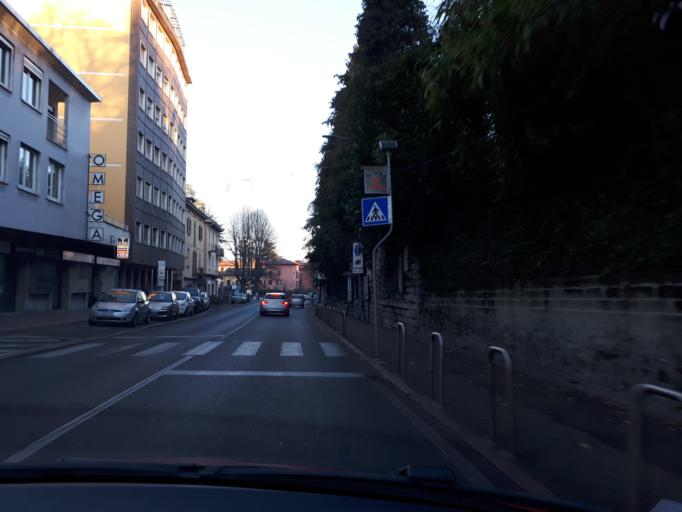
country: IT
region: Lombardy
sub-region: Provincia di Como
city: Fino Mornasco
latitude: 45.7452
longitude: 9.0502
